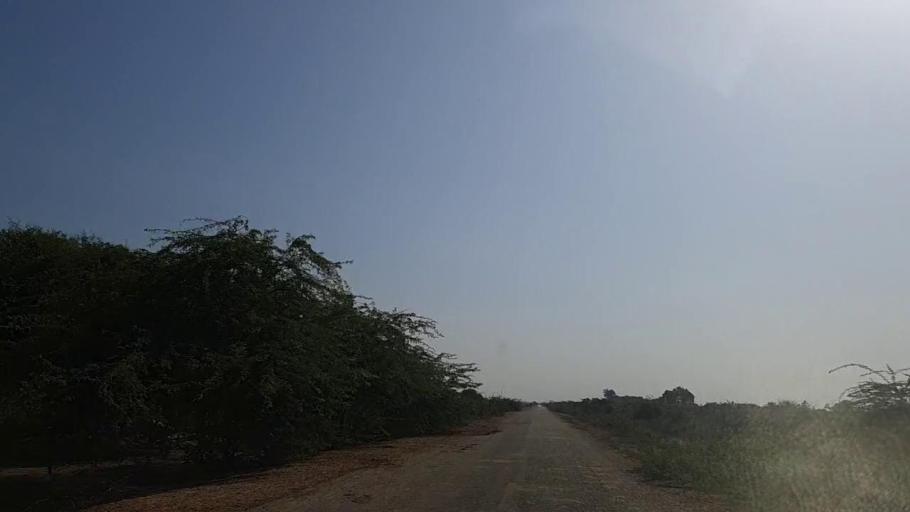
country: PK
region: Sindh
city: Jati
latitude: 24.4542
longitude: 68.2643
